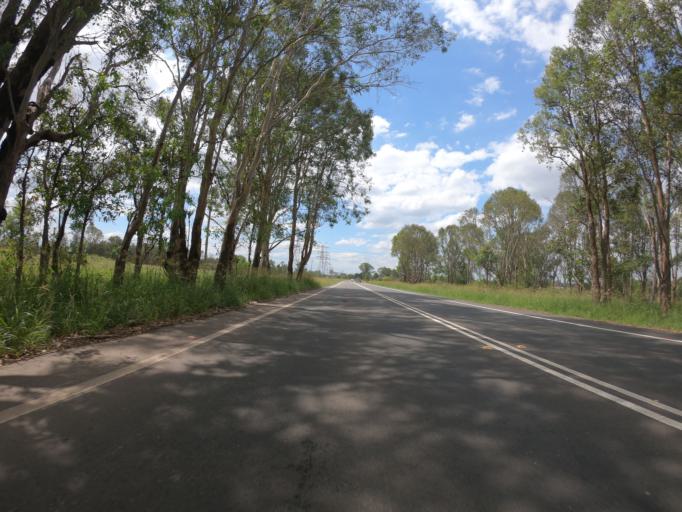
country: AU
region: New South Wales
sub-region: Penrith Municipality
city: Kingswood Park
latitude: -33.8157
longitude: 150.7601
